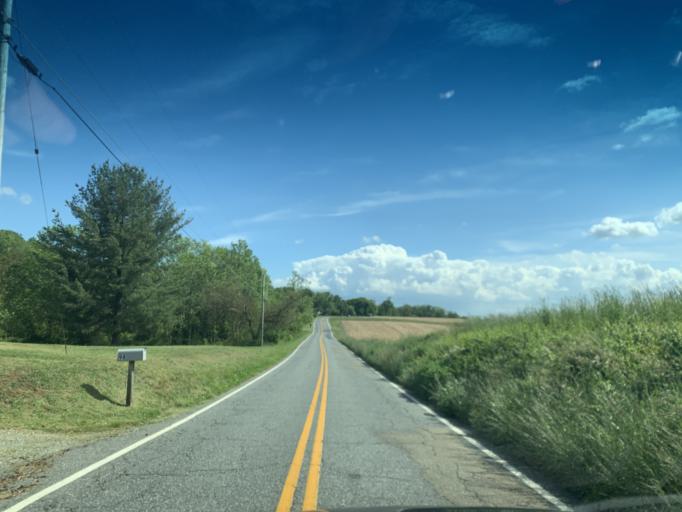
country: US
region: Maryland
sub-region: Cecil County
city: Rising Sun
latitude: 39.7123
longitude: -76.2023
